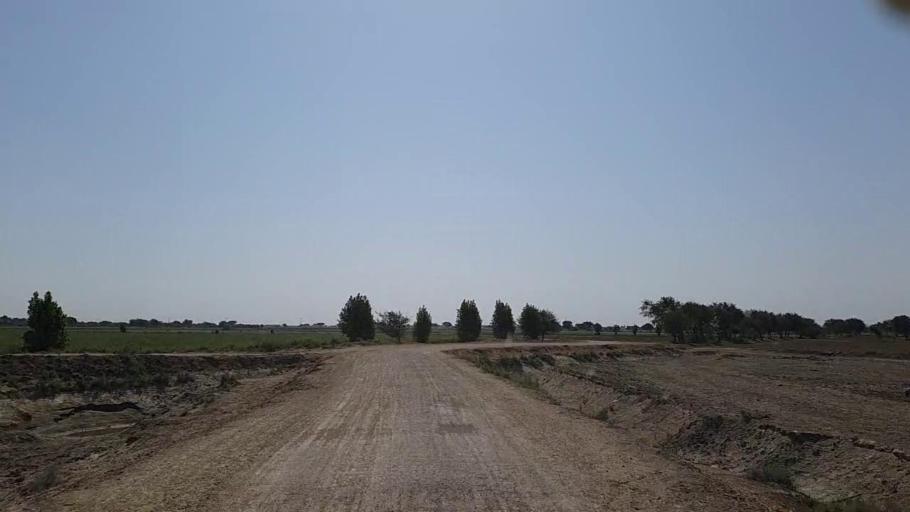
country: PK
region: Sindh
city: Mirpur Batoro
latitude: 24.6821
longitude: 68.2884
